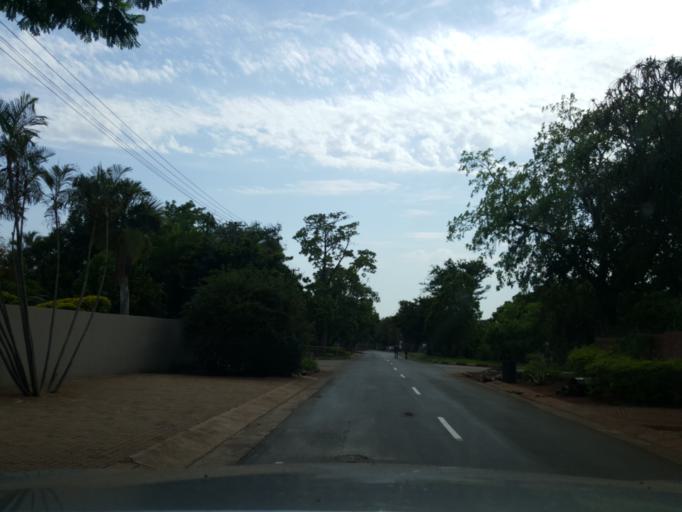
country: SZ
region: Hhohho
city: Ntfonjeni
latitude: -25.4939
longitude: 31.5105
